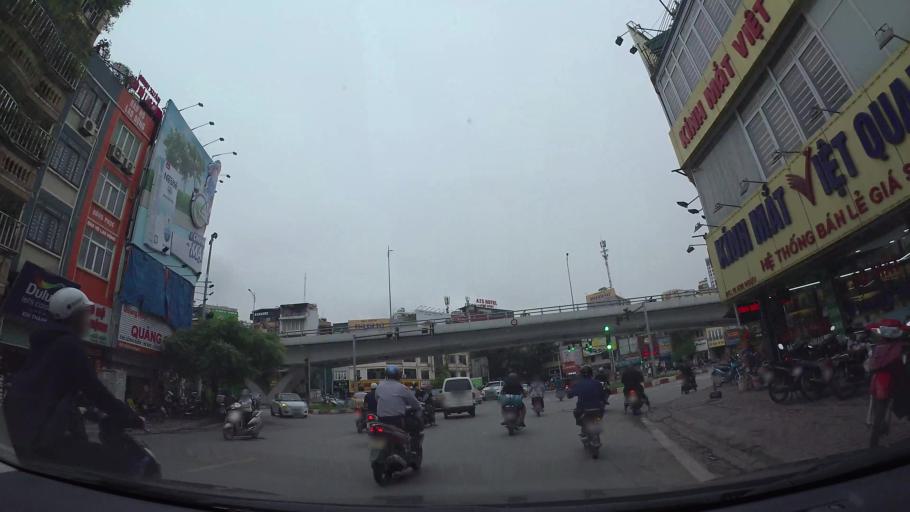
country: VN
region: Ha Noi
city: Hai BaTrung
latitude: 21.0086
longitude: 105.8607
